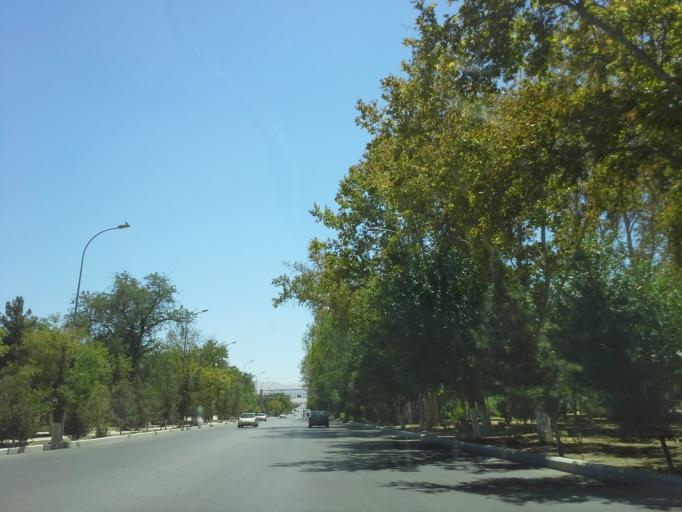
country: TM
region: Ahal
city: Ashgabat
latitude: 37.9165
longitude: 58.4060
